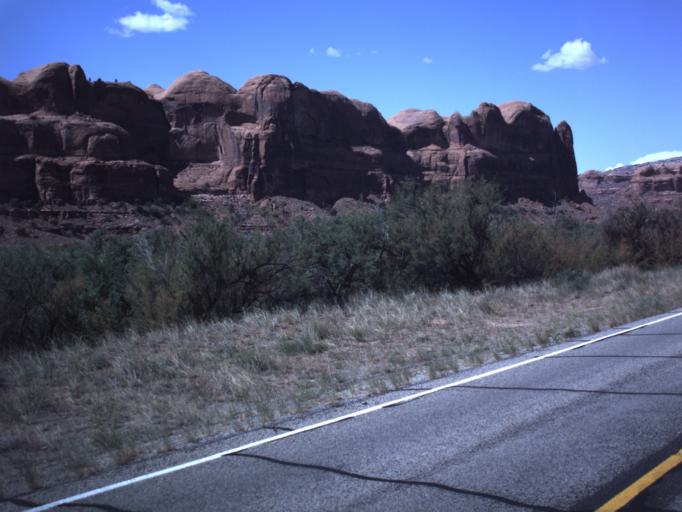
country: US
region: Utah
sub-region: Grand County
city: Moab
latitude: 38.5601
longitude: -109.6314
